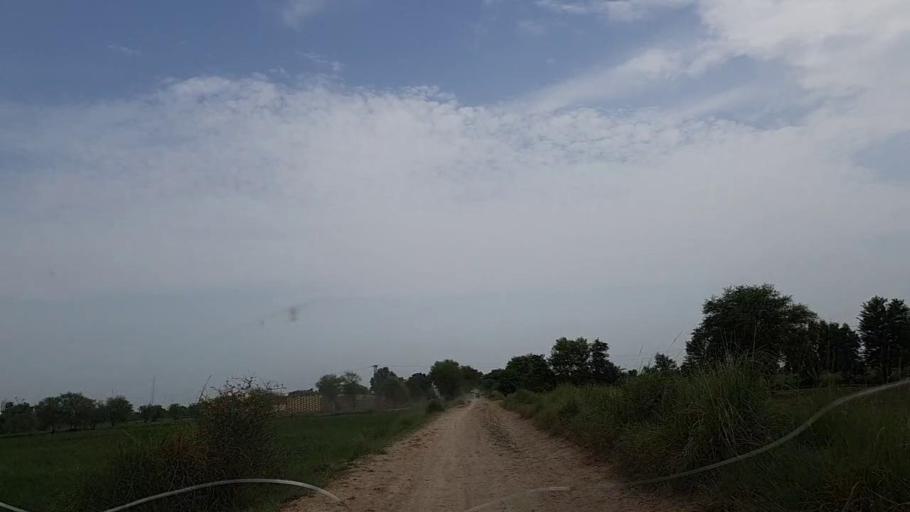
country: PK
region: Sindh
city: Tharu Shah
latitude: 26.8992
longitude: 68.0697
